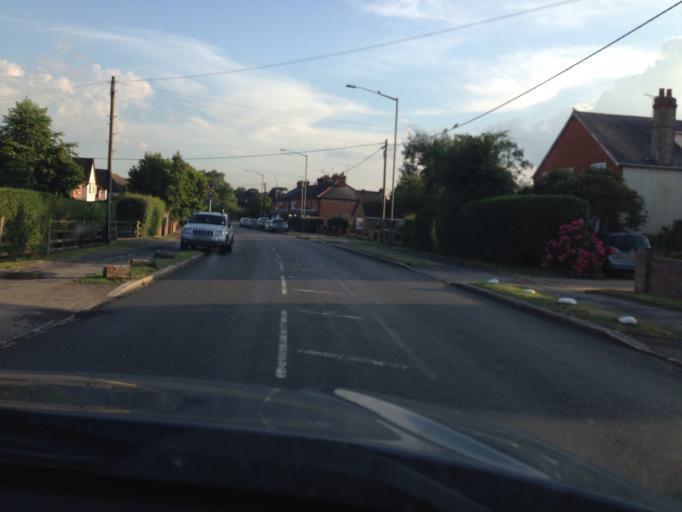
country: GB
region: England
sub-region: Buckinghamshire
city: Marlow
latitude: 51.5782
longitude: -0.7710
